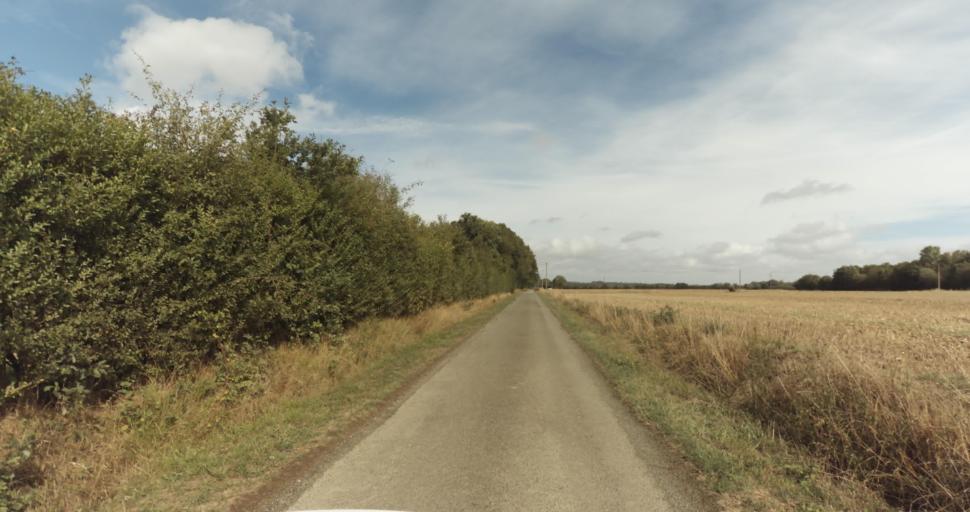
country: FR
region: Lower Normandy
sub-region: Departement de l'Orne
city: Gace
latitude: 48.8337
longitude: 0.3950
